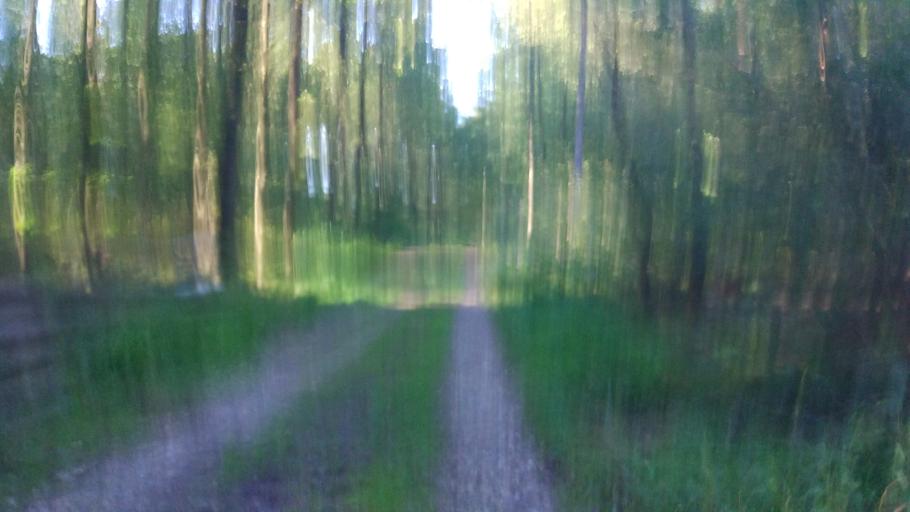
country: FR
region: Alsace
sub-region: Departement du Bas-Rhin
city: Gries
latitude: 48.7658
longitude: 7.8270
